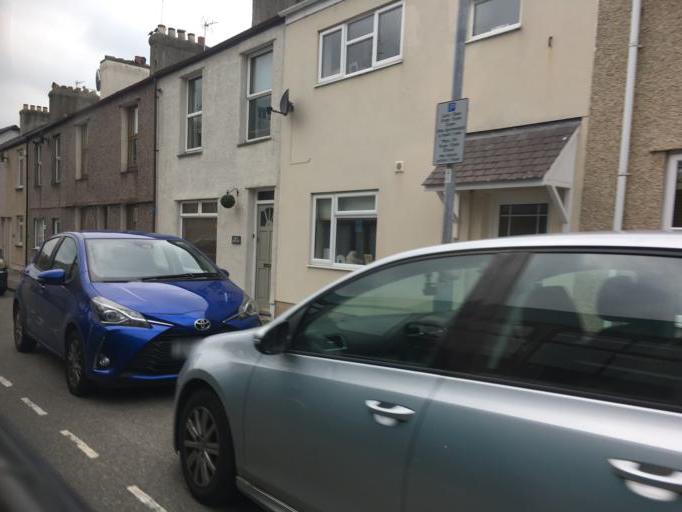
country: GB
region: Wales
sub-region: Gwynedd
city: Y Felinheli
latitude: 53.1847
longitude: -4.2089
